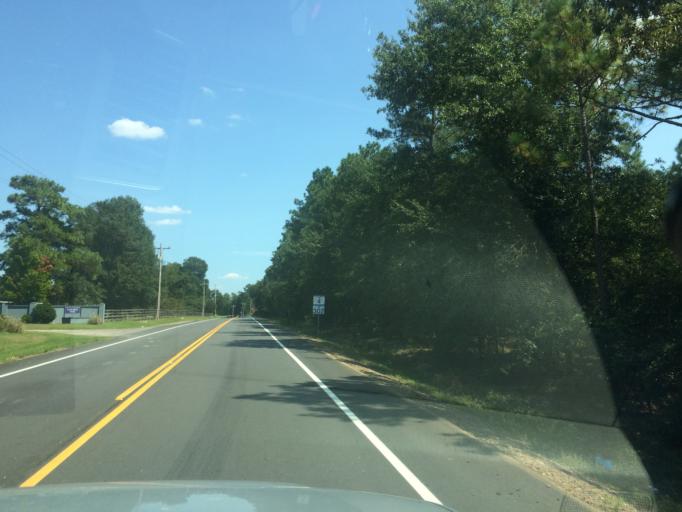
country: US
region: South Carolina
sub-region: Aiken County
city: Aiken
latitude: 33.5721
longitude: -81.5296
